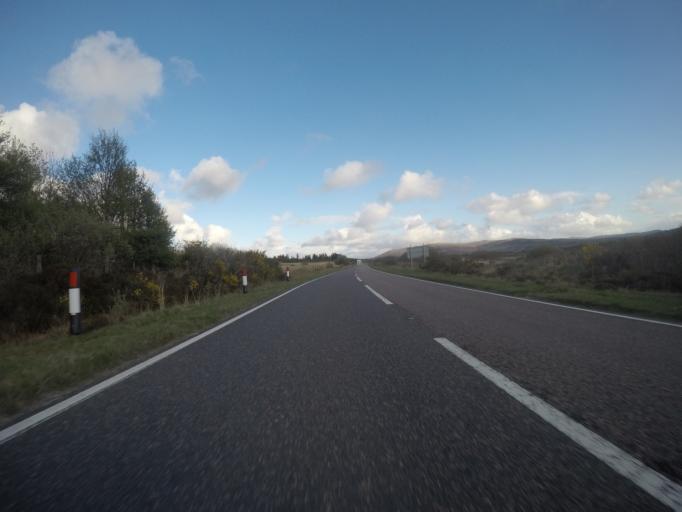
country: GB
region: Scotland
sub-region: Highland
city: Portree
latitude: 57.4573
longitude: -6.2731
